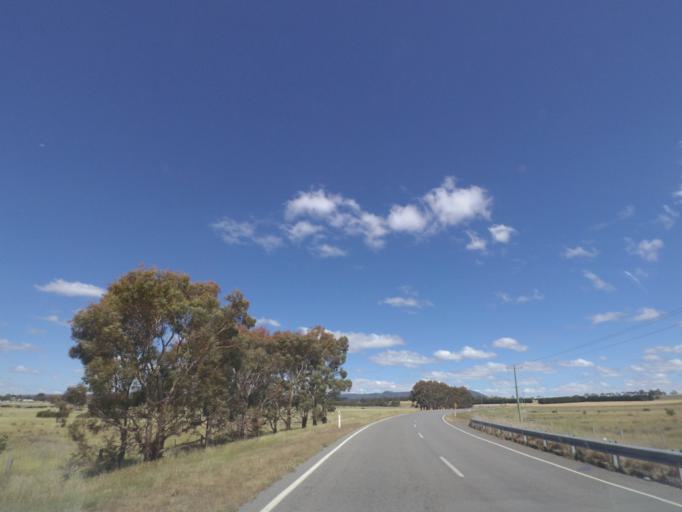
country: AU
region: Victoria
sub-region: Mount Alexander
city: Castlemaine
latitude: -37.2927
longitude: 144.4971
